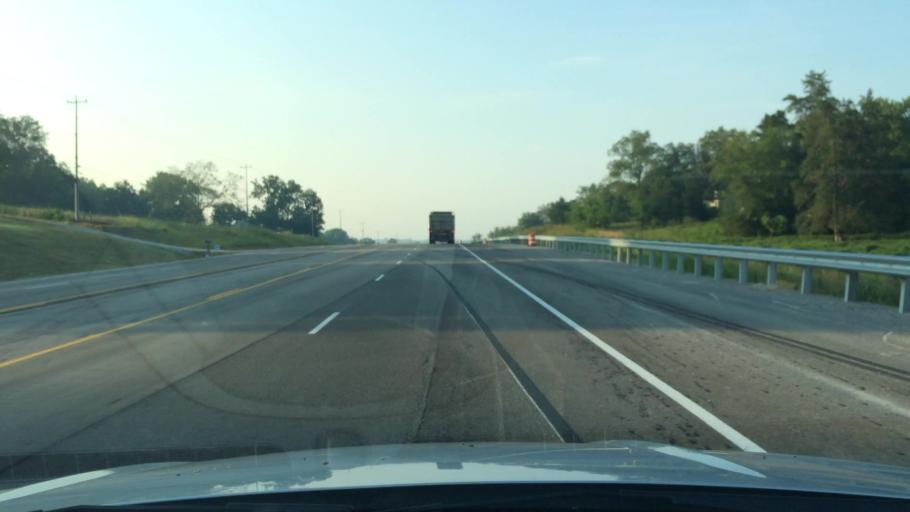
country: US
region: Tennessee
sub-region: Giles County
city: Pulaski
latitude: 35.1651
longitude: -87.0125
